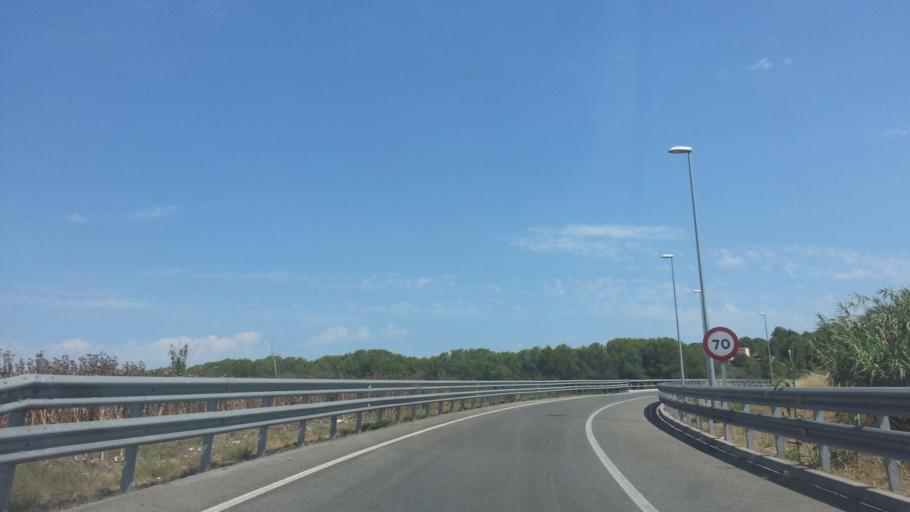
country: ES
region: Catalonia
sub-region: Provincia de Barcelona
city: Vilafranca del Penedes
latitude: 41.3342
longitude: 1.7118
